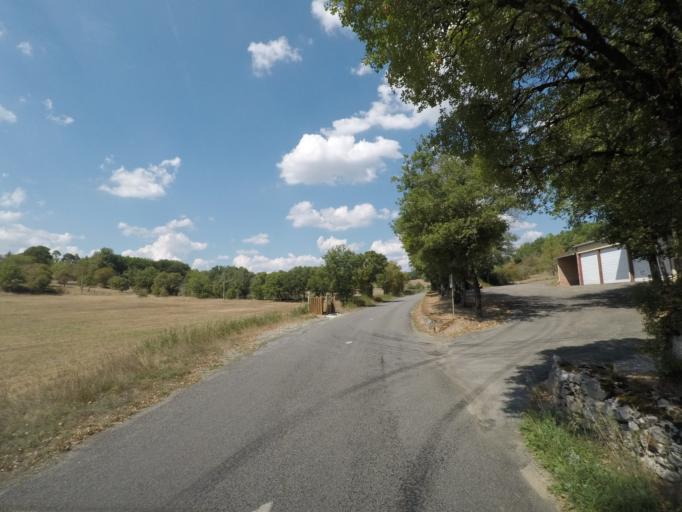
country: FR
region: Midi-Pyrenees
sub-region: Departement du Lot
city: Cahors
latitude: 44.5560
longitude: 1.5843
